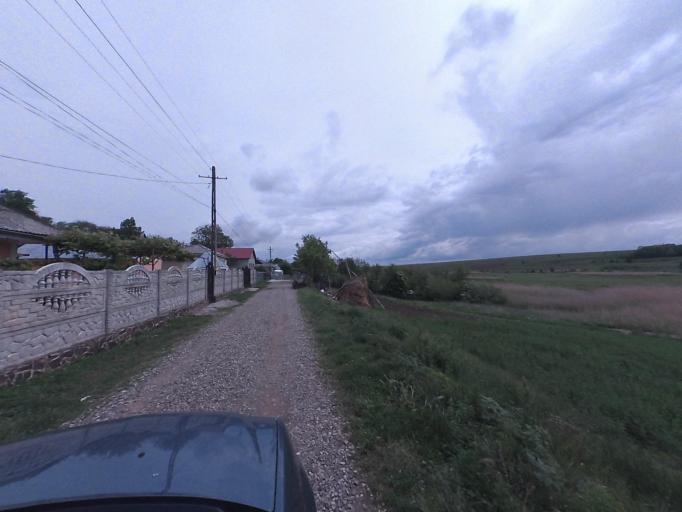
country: RO
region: Neamt
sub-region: Comuna Dulcesti
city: Dulcesti
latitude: 46.9550
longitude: 26.7994
